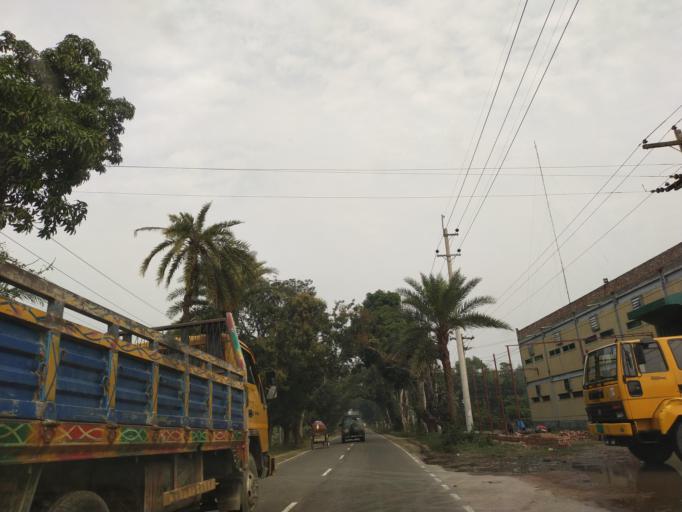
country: BD
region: Dhaka
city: Narsingdi
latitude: 23.9971
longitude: 90.7378
